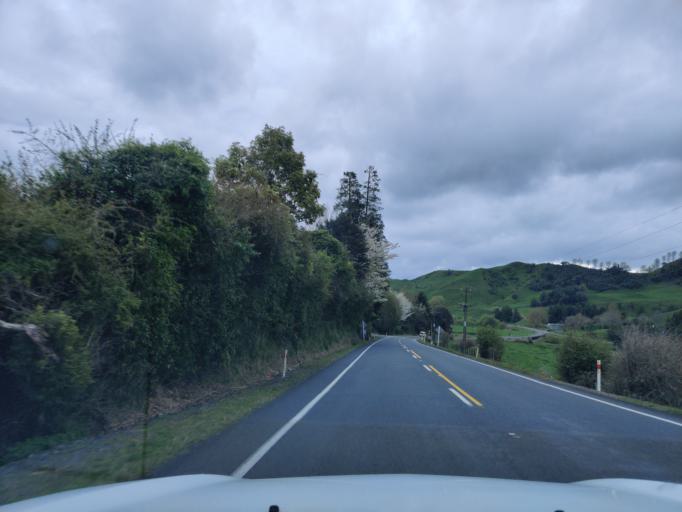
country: NZ
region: Waikato
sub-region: Otorohanga District
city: Otorohanga
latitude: -38.4917
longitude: 175.1887
